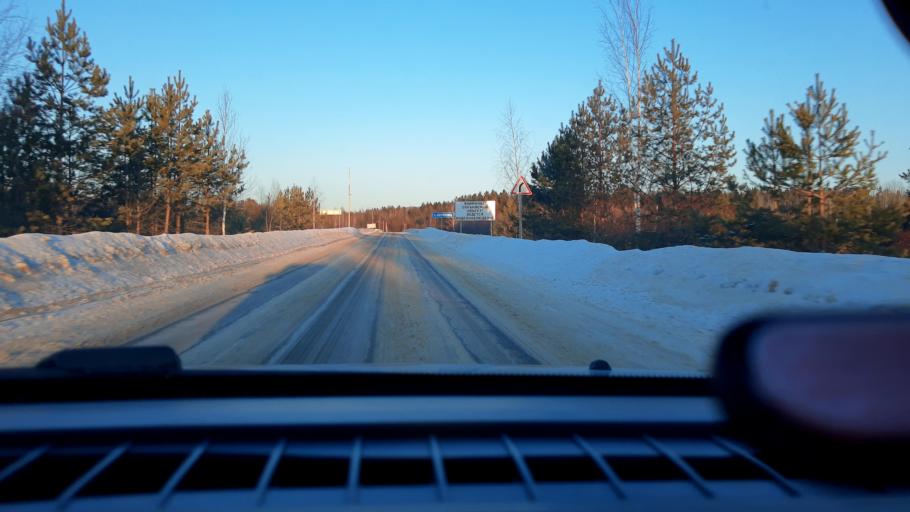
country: RU
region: Nizjnij Novgorod
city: Lyskovo
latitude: 56.1557
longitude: 44.9448
